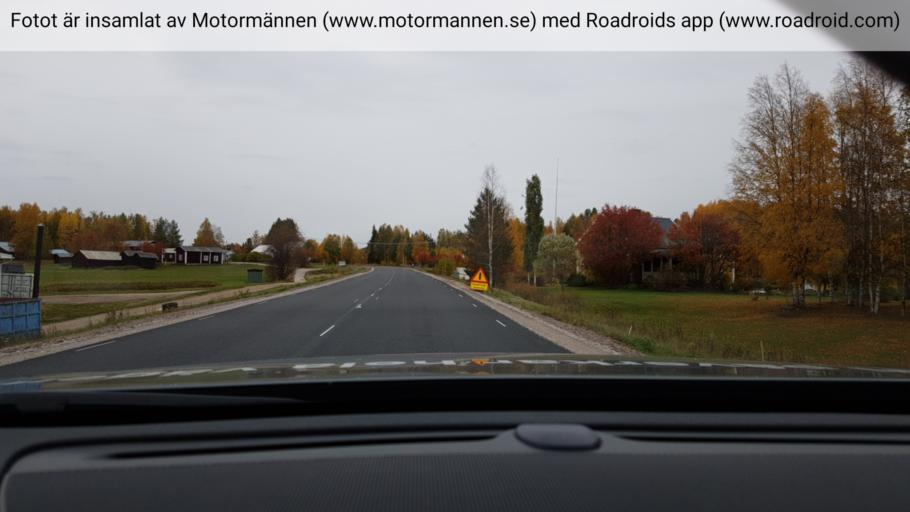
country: SE
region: Norrbotten
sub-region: Overkalix Kommun
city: OEverkalix
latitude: 66.3661
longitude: 22.8415
